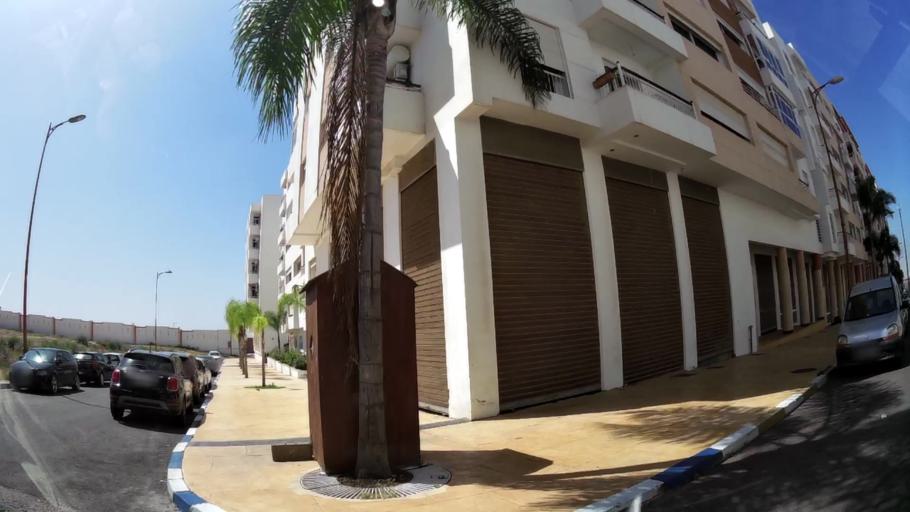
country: MA
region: Oued ed Dahab-Lagouira
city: Dakhla
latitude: 30.4344
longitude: -9.5699
